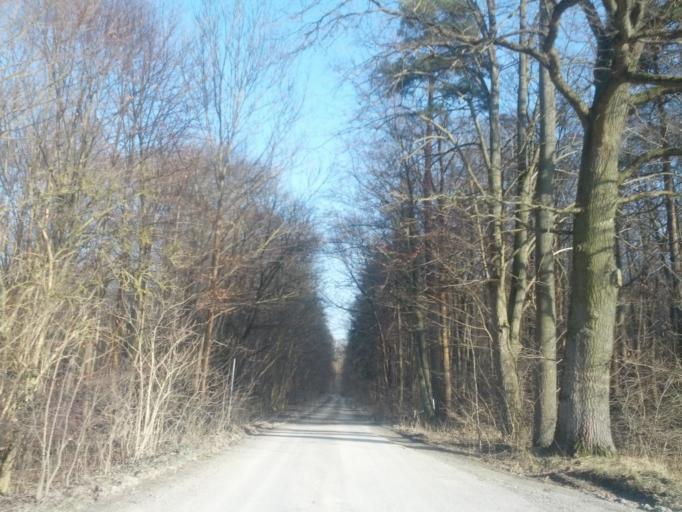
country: DE
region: Thuringia
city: Frankenroda
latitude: 51.0844
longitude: 10.2746
